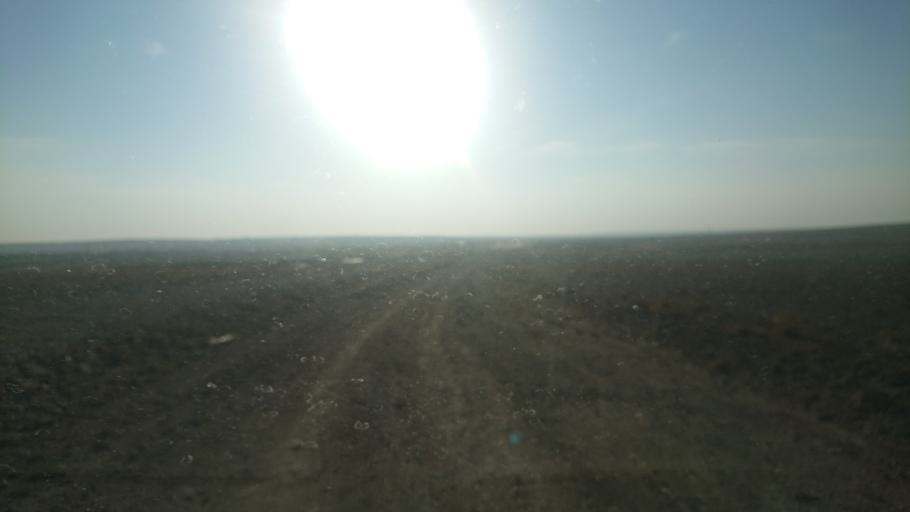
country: TR
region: Aksaray
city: Sultanhani
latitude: 38.1428
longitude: 33.5752
